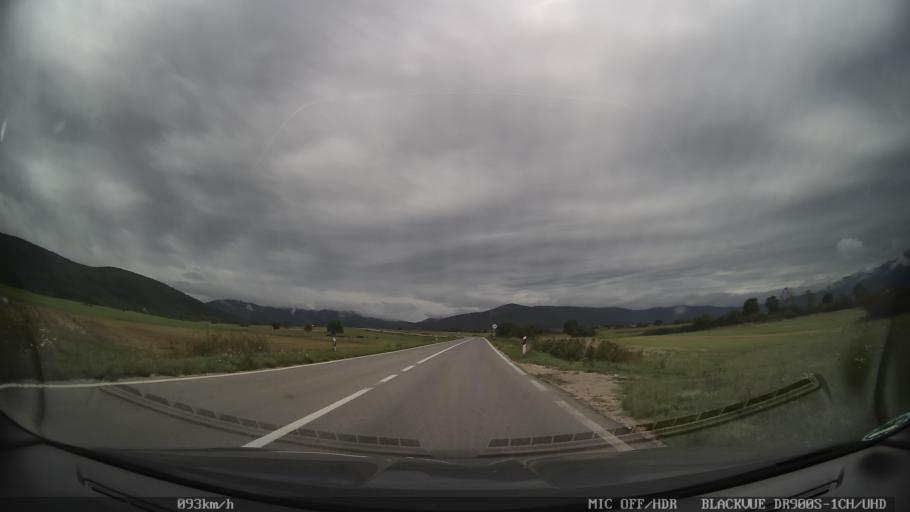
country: HR
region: Licko-Senjska
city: Otocac
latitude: 44.8561
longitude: 15.2790
